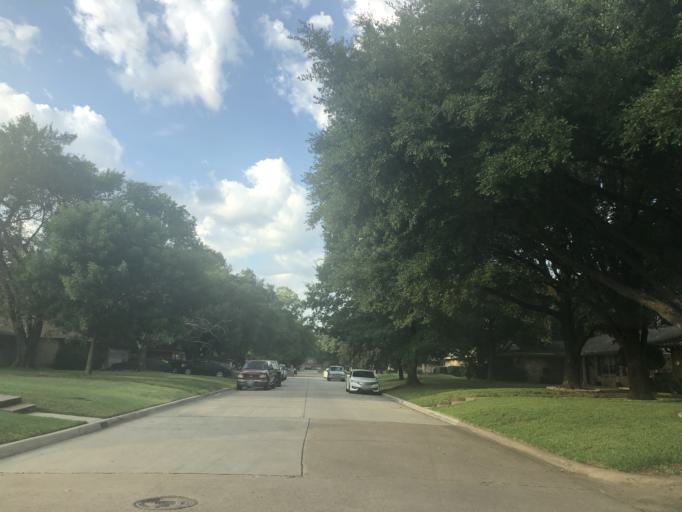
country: US
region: Texas
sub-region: Dallas County
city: Grand Prairie
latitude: 32.7670
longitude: -97.0135
